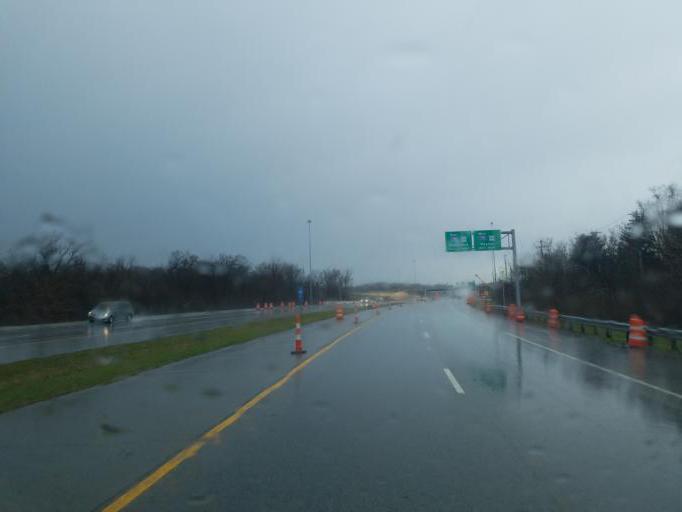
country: US
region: Ohio
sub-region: Franklin County
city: Worthington
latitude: 40.1181
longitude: -83.0345
